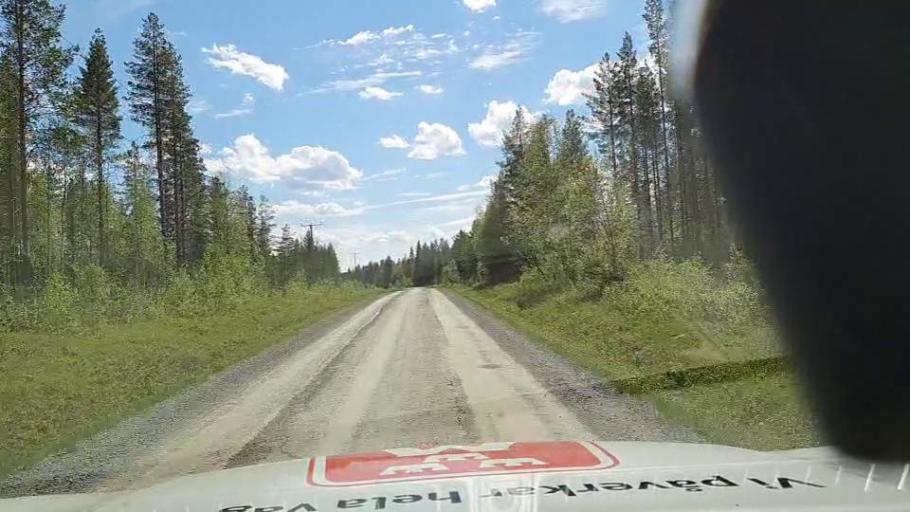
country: SE
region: Jaemtland
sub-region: Stroemsunds Kommun
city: Stroemsund
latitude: 64.4628
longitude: 15.5929
